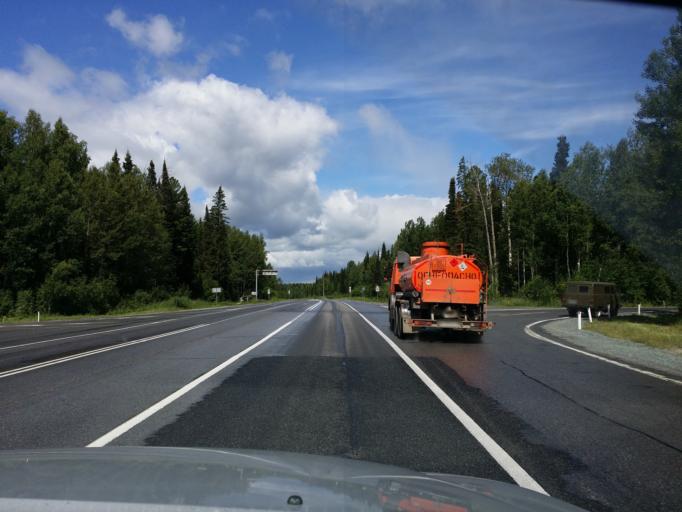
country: RU
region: Tjumen
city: Turtas
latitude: 58.6172
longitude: 68.7637
